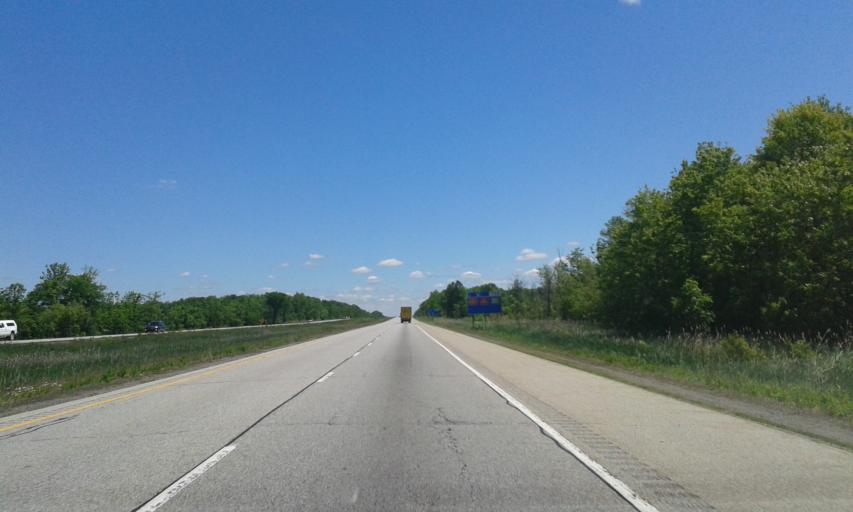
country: US
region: New York
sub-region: St. Lawrence County
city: Norfolk
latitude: 44.9013
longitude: -75.2348
